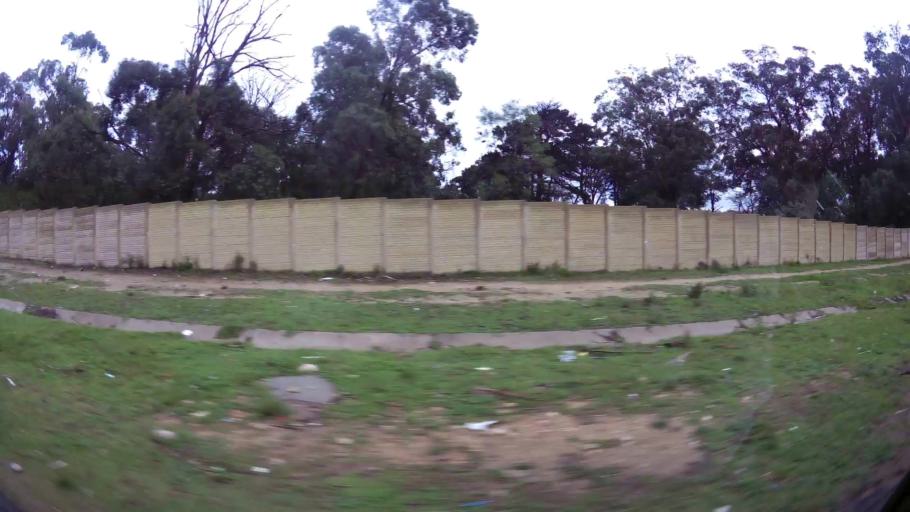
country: ZA
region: Eastern Cape
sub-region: Nelson Mandela Bay Metropolitan Municipality
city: Port Elizabeth
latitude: -33.9920
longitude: 25.5795
